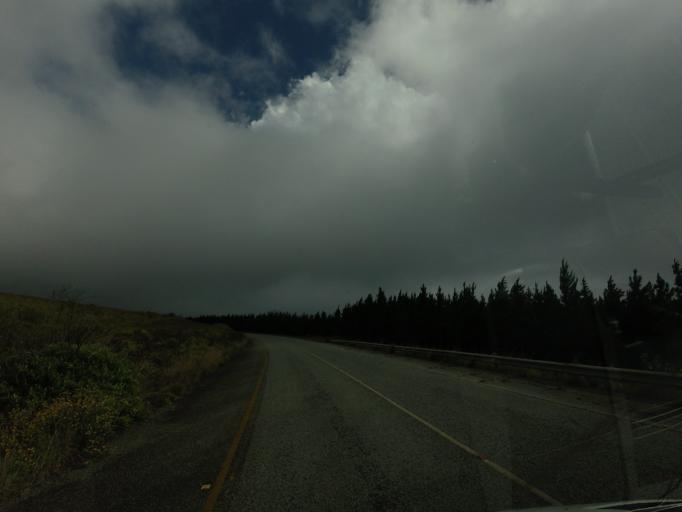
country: ZA
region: Mpumalanga
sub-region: Ehlanzeni District
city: Graksop
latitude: -24.8605
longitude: 30.8902
